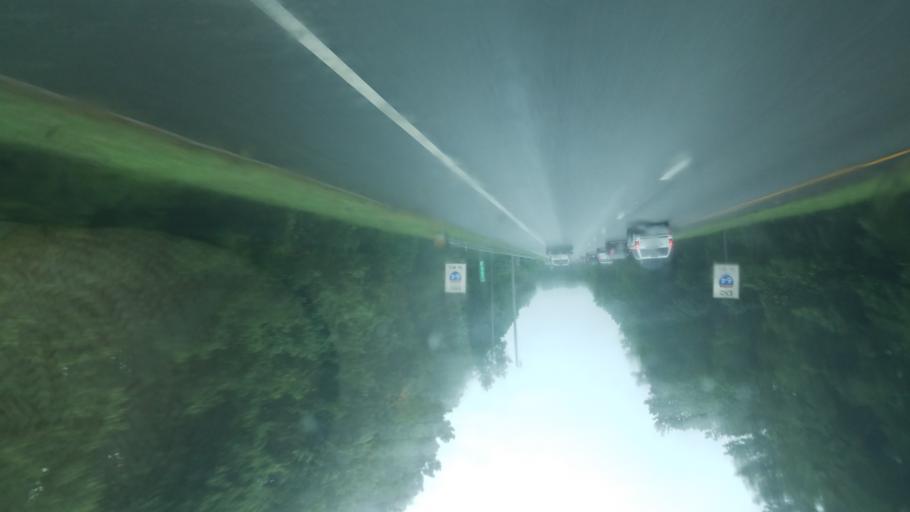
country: US
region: Virginia
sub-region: City of Portsmouth
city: Portsmouth Heights
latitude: 36.7780
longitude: -76.3825
